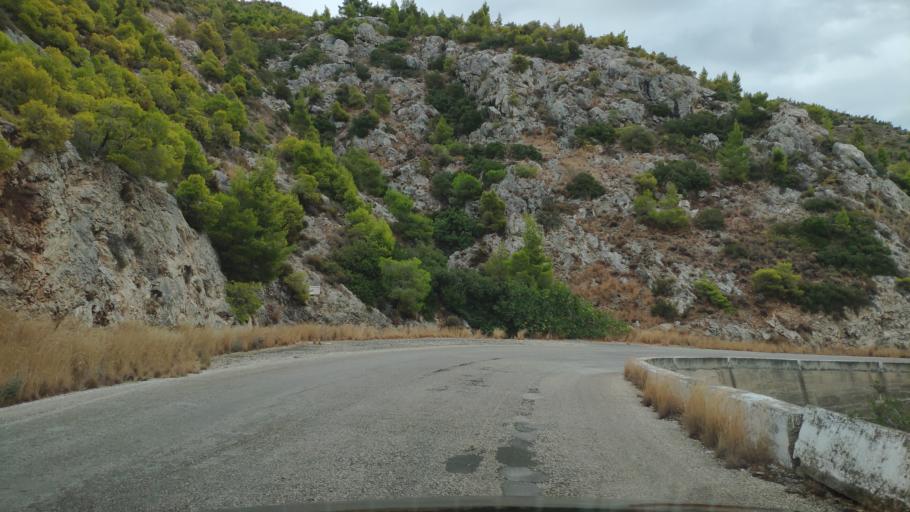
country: GR
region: Peloponnese
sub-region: Nomos Korinthias
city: Perachora
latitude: 37.9979
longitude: 22.9485
